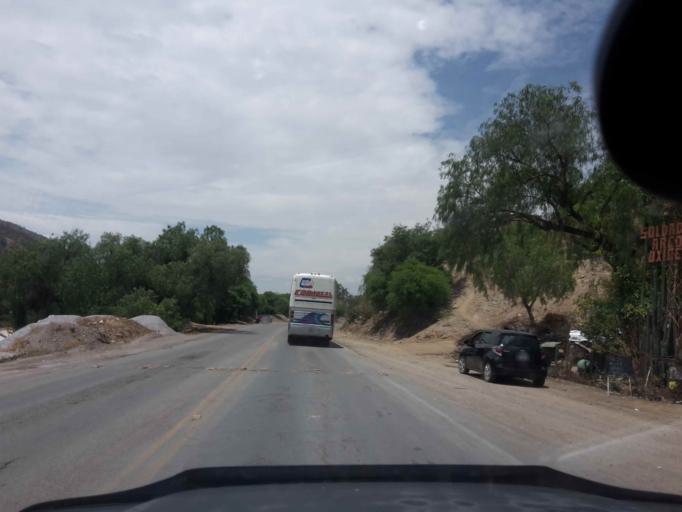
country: BO
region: Cochabamba
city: Sipe Sipe
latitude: -17.5560
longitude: -66.3426
